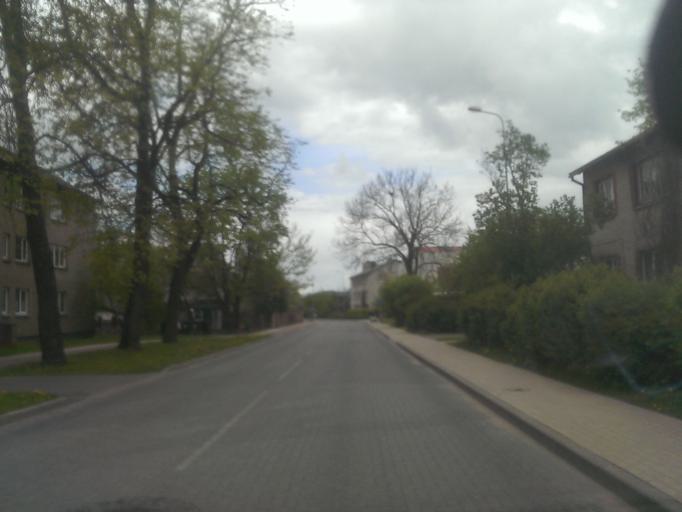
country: LV
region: Kuldigas Rajons
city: Kuldiga
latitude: 56.9704
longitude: 21.9599
